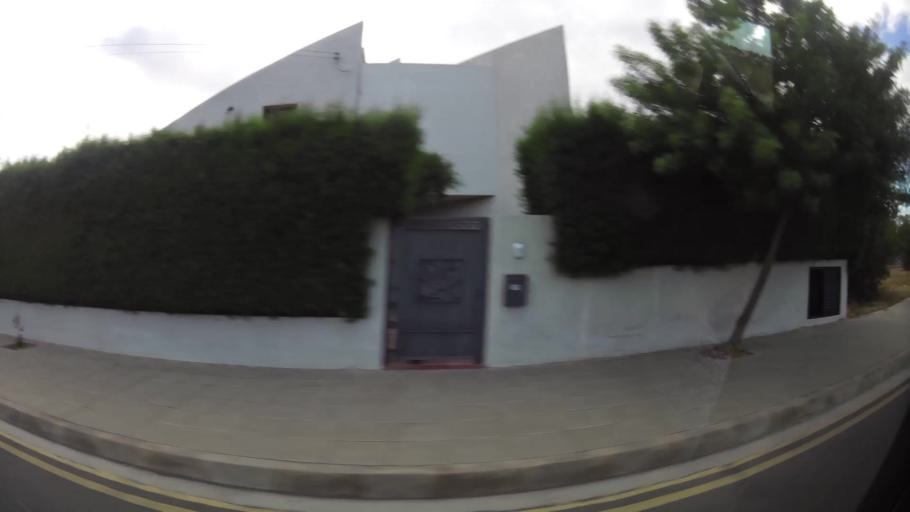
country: CY
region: Lefkosia
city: Nicosia
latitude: 35.1458
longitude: 33.3332
